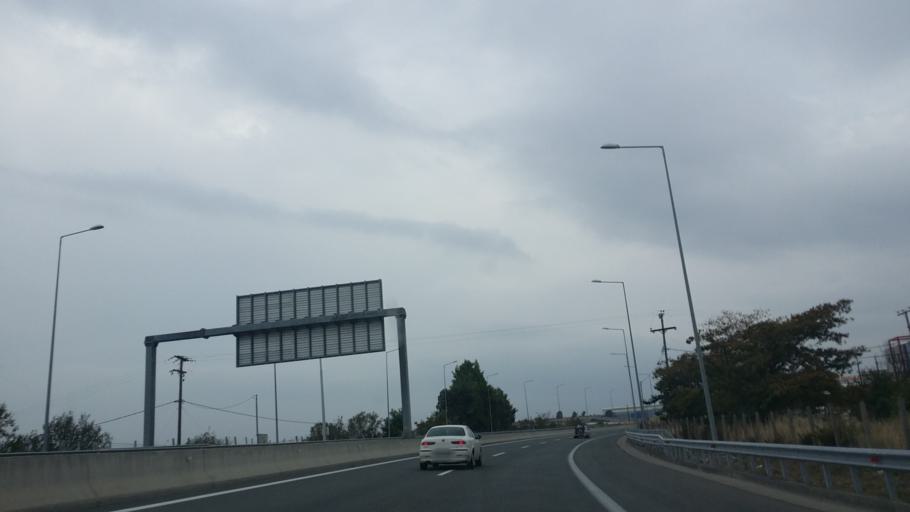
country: GR
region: Central Greece
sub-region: Nomos Voiotias
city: Arma
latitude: 38.3802
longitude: 23.4981
